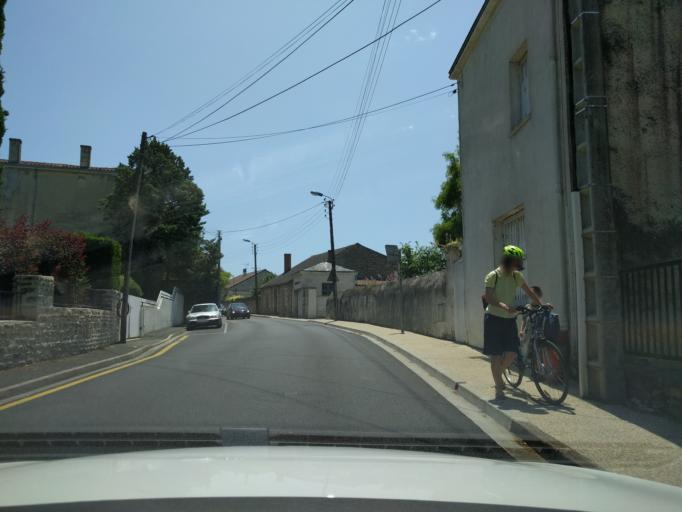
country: FR
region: Poitou-Charentes
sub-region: Departement des Deux-Sevres
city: Niort
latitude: 46.3338
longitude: -0.4616
